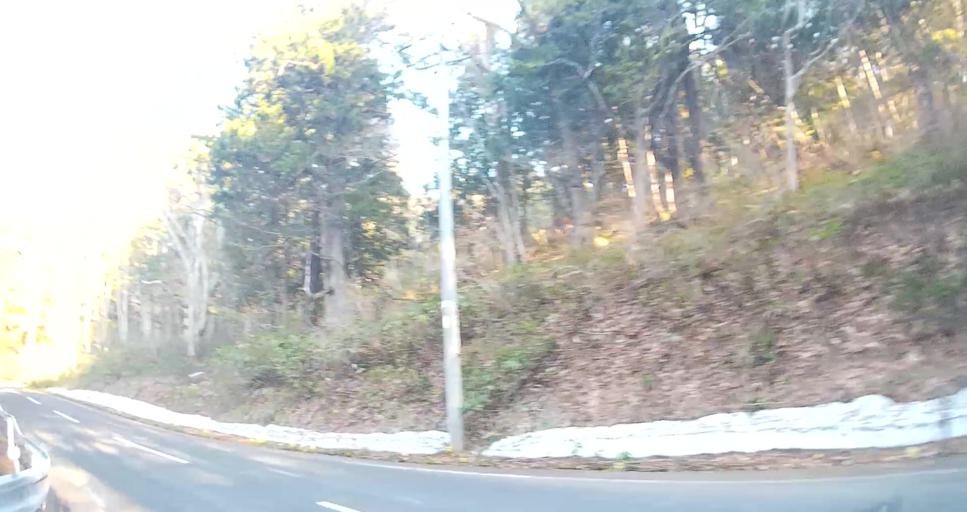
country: JP
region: Aomori
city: Mutsu
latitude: 41.3146
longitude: 141.1127
